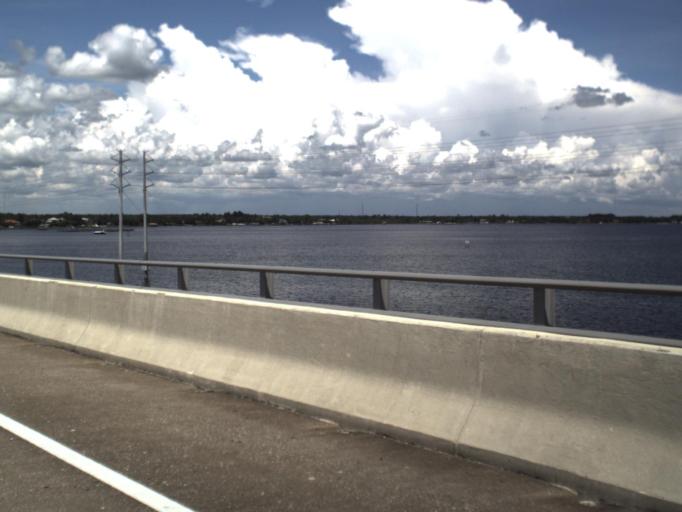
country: US
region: Florida
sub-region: Charlotte County
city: Charlotte Harbor
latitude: 26.9462
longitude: -82.0576
